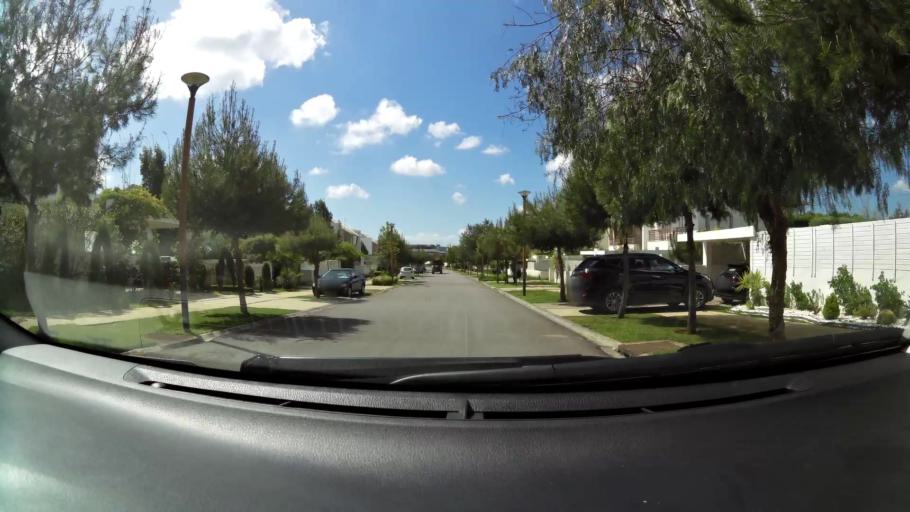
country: MA
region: Grand Casablanca
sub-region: Mediouna
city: Mediouna
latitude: 33.4907
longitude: -7.5855
